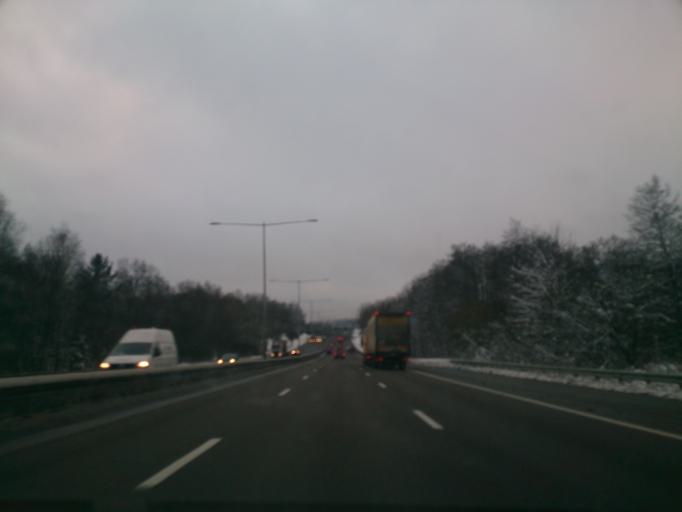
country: SE
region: Stockholm
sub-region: Botkyrka Kommun
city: Eriksberg
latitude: 59.2347
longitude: 17.8097
